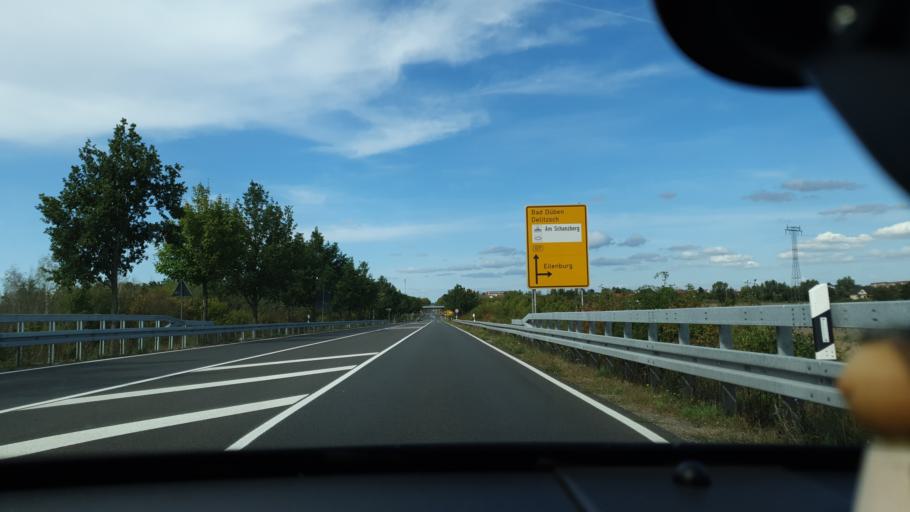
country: DE
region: Saxony
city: Eilenburg
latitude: 51.4461
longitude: 12.6135
